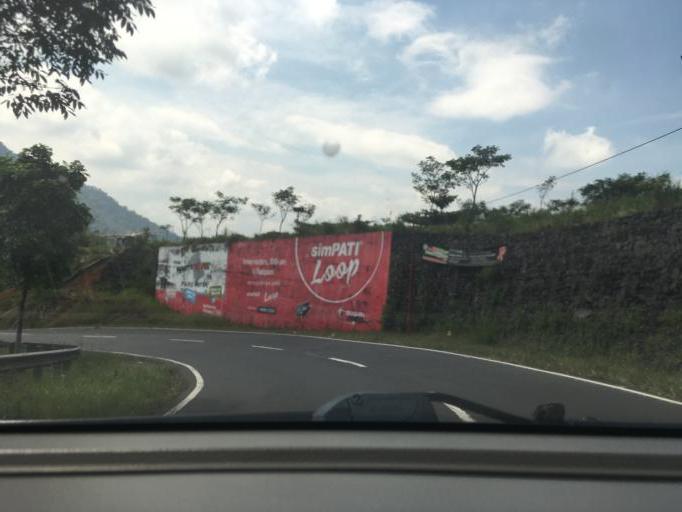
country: ID
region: West Java
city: Wage Cibahayu
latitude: -7.1149
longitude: 108.1146
